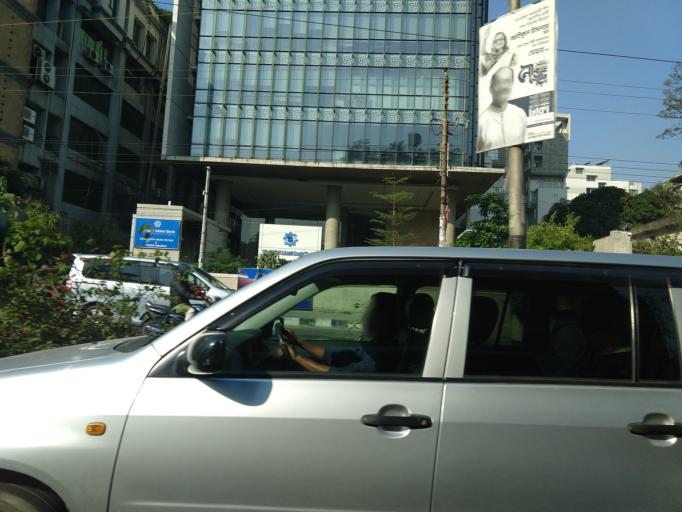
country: BD
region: Dhaka
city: Paltan
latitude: 23.7890
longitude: 90.4164
